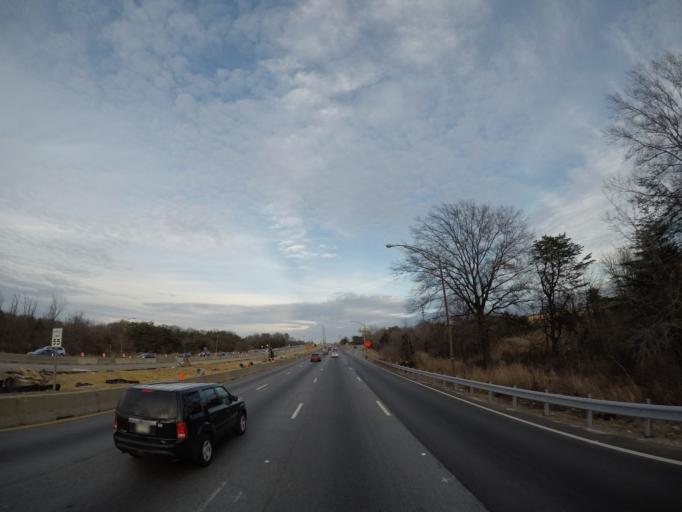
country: US
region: Maryland
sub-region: Prince George's County
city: Morningside
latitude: 38.8197
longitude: -76.8940
